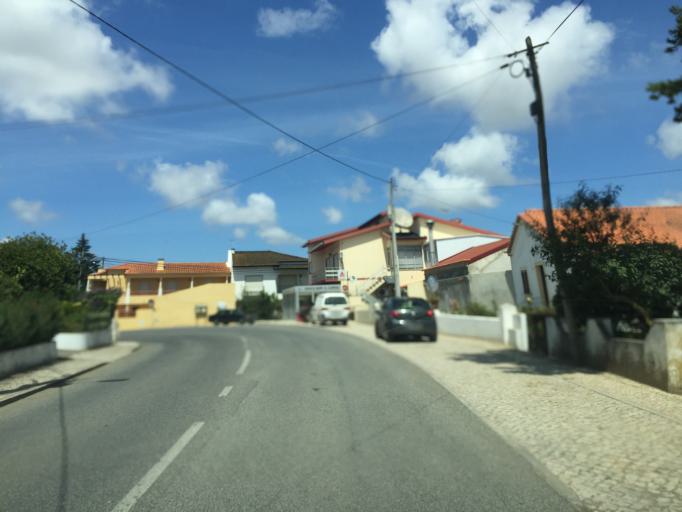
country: PT
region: Lisbon
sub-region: Lourinha
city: Lourinha
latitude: 39.2752
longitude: -9.2773
